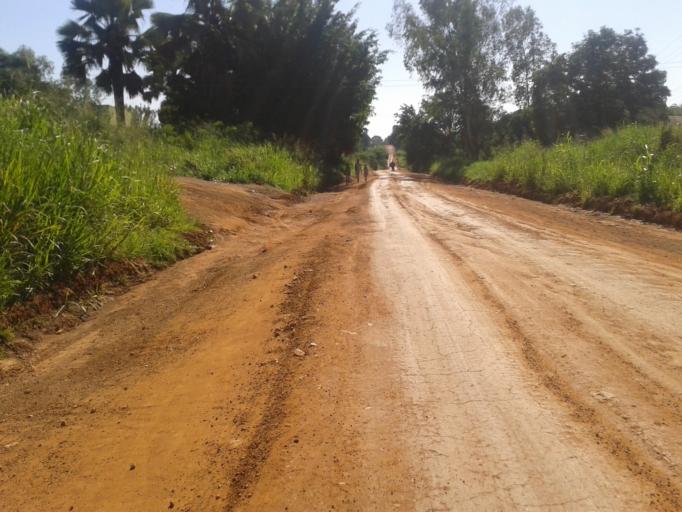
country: UG
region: Northern Region
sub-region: Gulu District
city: Gulu
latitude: 2.7936
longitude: 32.3085
